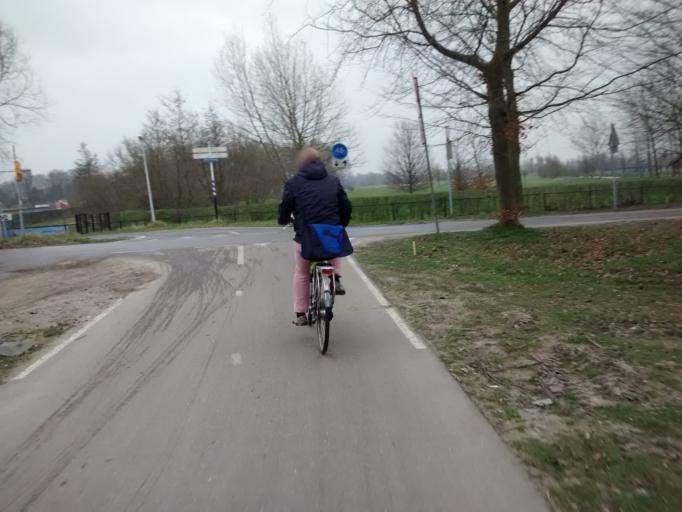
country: NL
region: Utrecht
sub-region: Gemeente Utrecht
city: Lunetten
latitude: 52.0674
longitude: 5.1489
